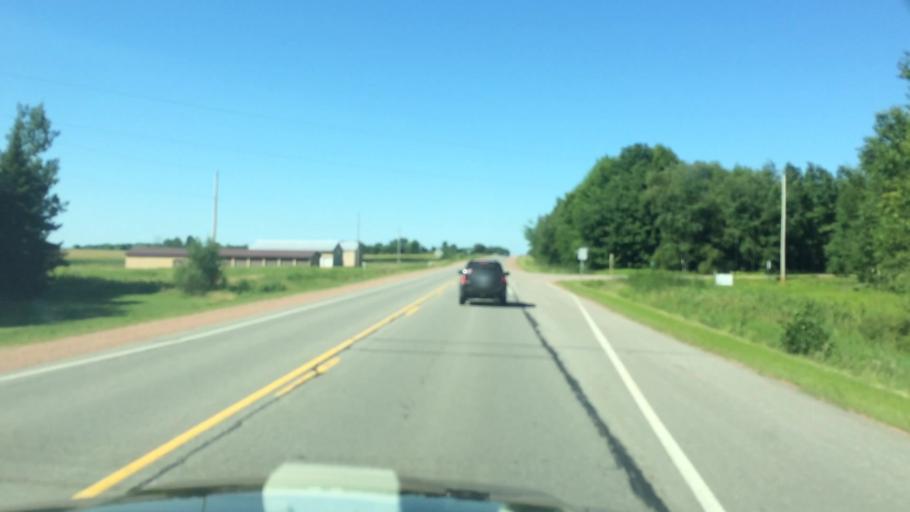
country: US
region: Wisconsin
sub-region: Marathon County
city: Stratford
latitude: 44.7213
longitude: -90.1008
